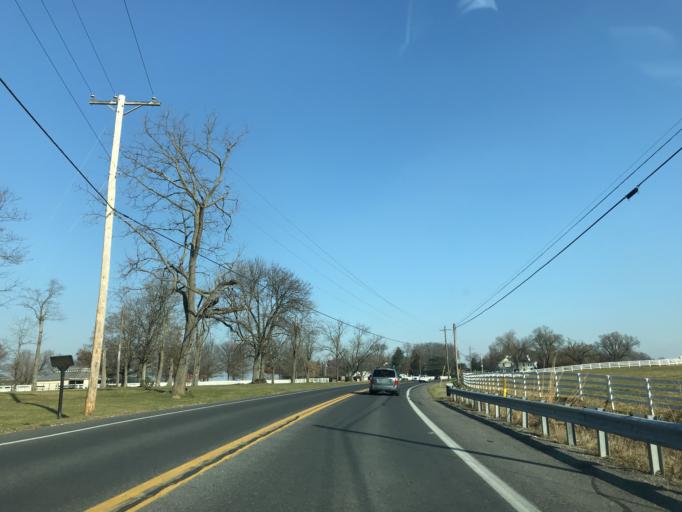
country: US
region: Pennsylvania
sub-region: York County
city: Pennville
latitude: 39.7671
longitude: -77.0256
